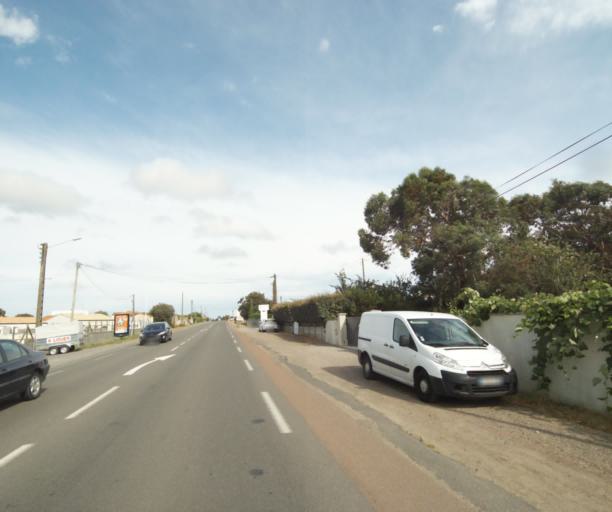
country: FR
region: Pays de la Loire
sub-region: Departement de la Vendee
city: Chateau-d'Olonne
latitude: 46.4826
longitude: -1.7208
